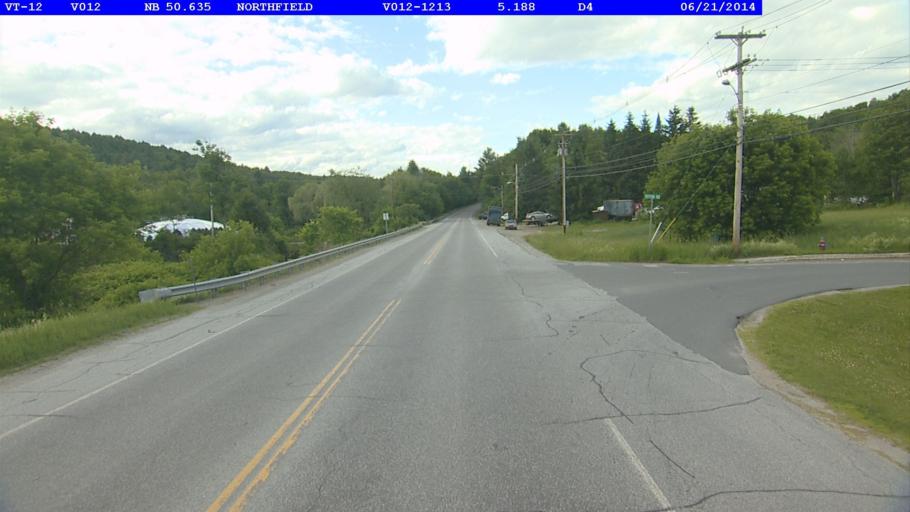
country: US
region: Vermont
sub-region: Washington County
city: Northfield
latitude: 44.1631
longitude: -72.6561
